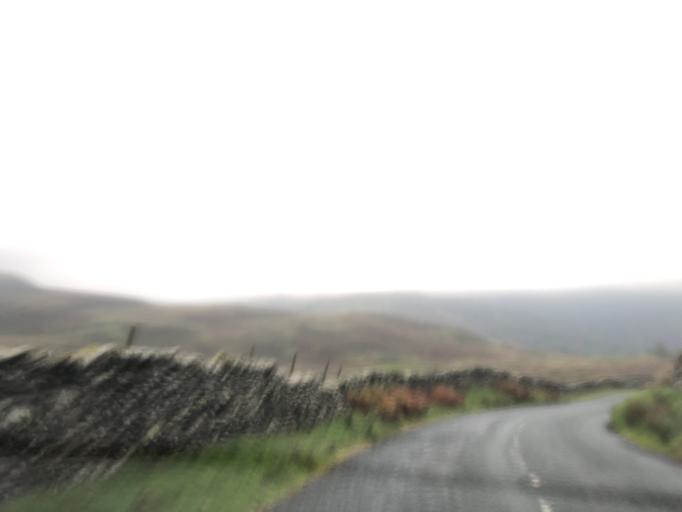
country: GB
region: England
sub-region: Cumbria
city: Ambleside
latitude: 54.4524
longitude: -2.9135
